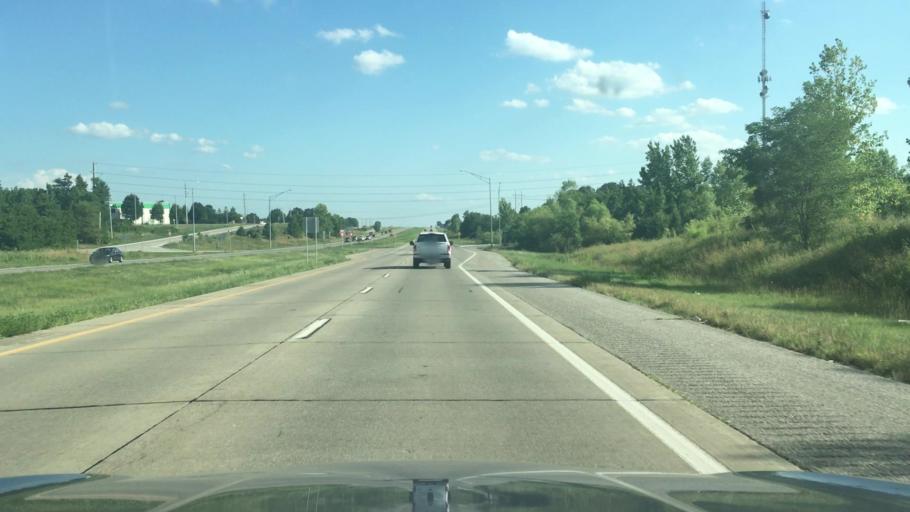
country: US
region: Missouri
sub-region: Jackson County
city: Greenwood
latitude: 38.8686
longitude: -94.3751
